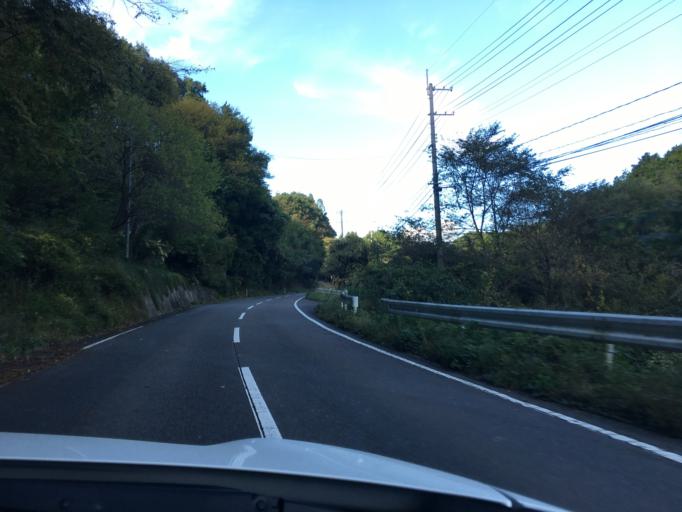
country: JP
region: Fukushima
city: Ishikawa
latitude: 37.1963
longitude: 140.4586
